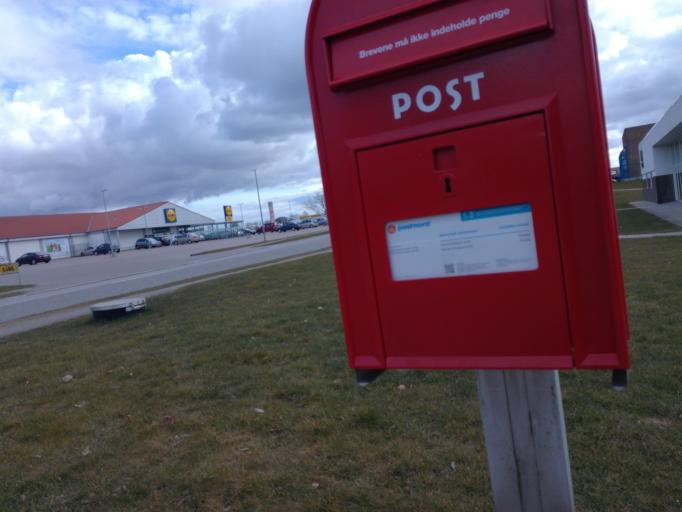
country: DK
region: South Denmark
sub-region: Fredericia Kommune
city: Fredericia
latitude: 55.5704
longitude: 9.7176
